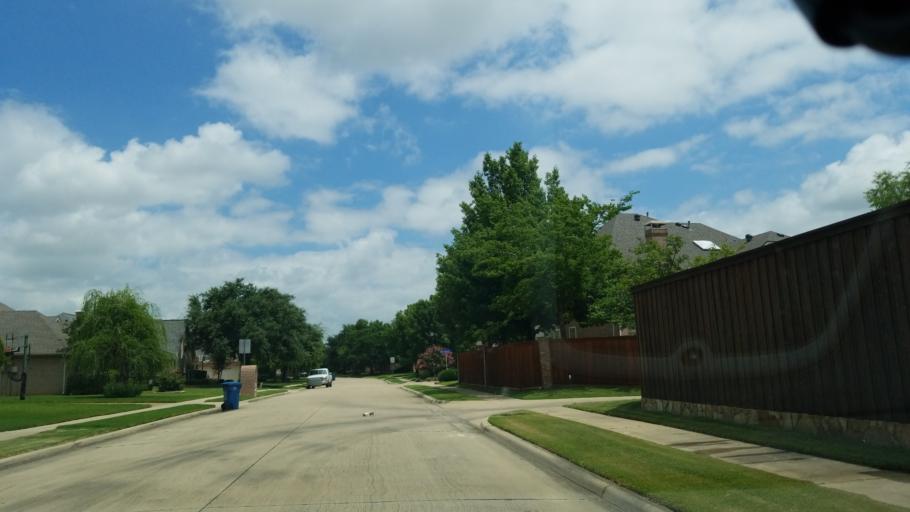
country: US
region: Texas
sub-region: Dallas County
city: Carrollton
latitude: 32.9574
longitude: -96.9526
